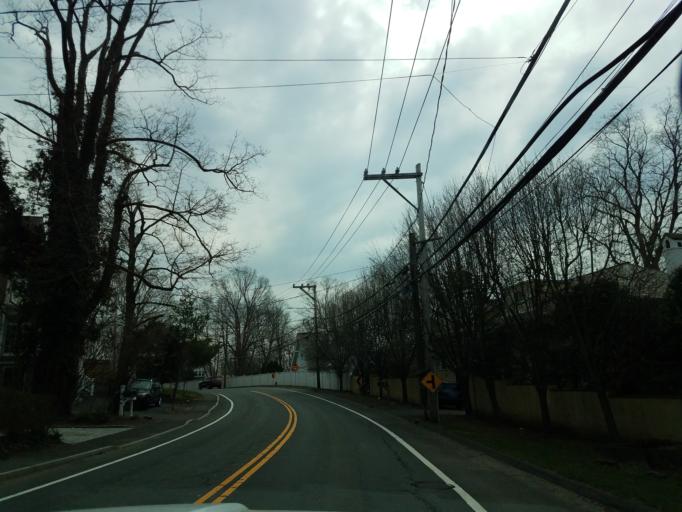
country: US
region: Connecticut
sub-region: Fairfield County
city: Greenwich
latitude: 41.0342
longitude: -73.6337
